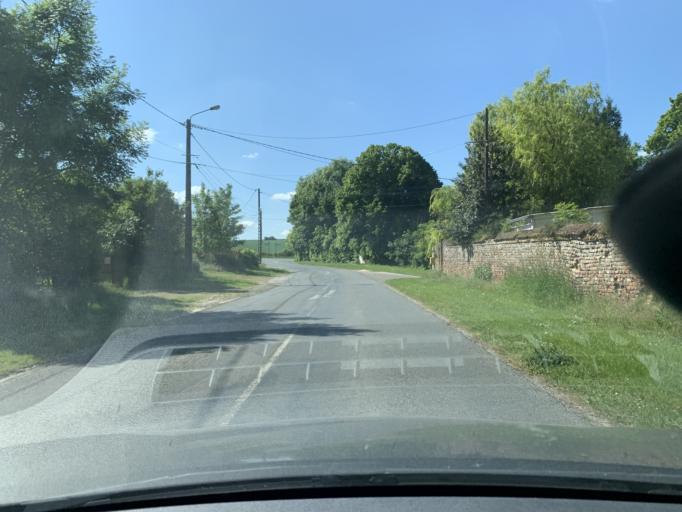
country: FR
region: Nord-Pas-de-Calais
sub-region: Departement du Pas-de-Calais
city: Oisy-le-Verger
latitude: 50.2617
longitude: 3.1404
